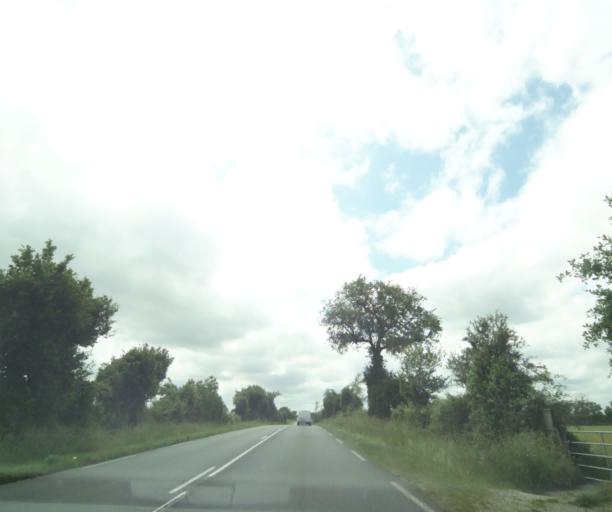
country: FR
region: Poitou-Charentes
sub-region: Departement des Deux-Sevres
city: Viennay
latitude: 46.7177
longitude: -0.2389
